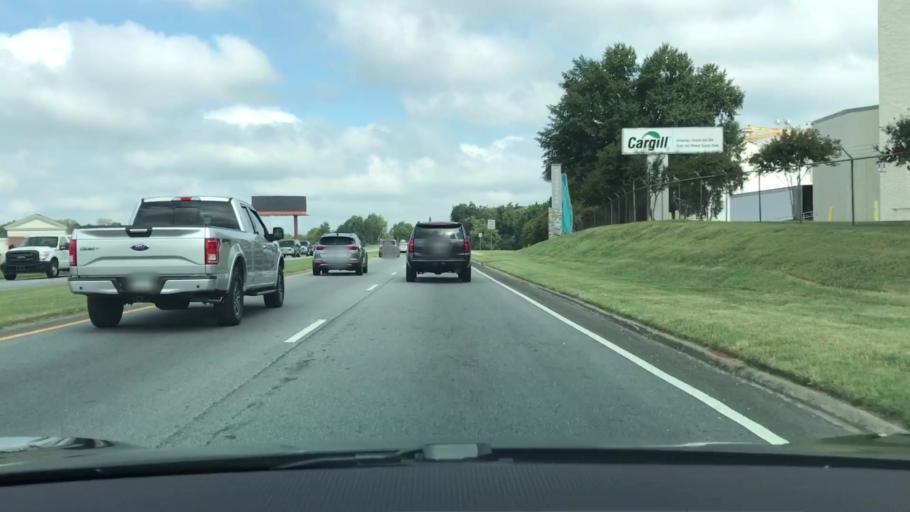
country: US
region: Georgia
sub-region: Hall County
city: Gainesville
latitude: 34.2891
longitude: -83.8123
